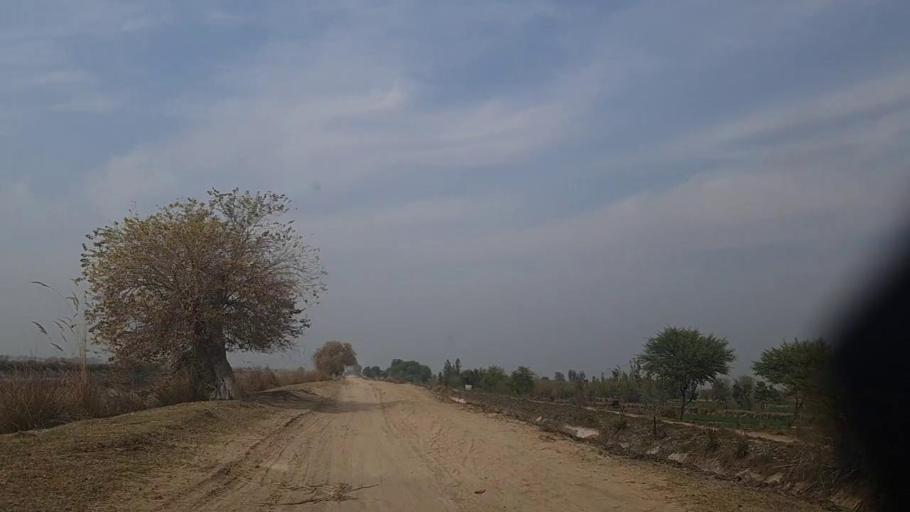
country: PK
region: Sindh
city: Daur
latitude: 26.3256
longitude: 68.1944
